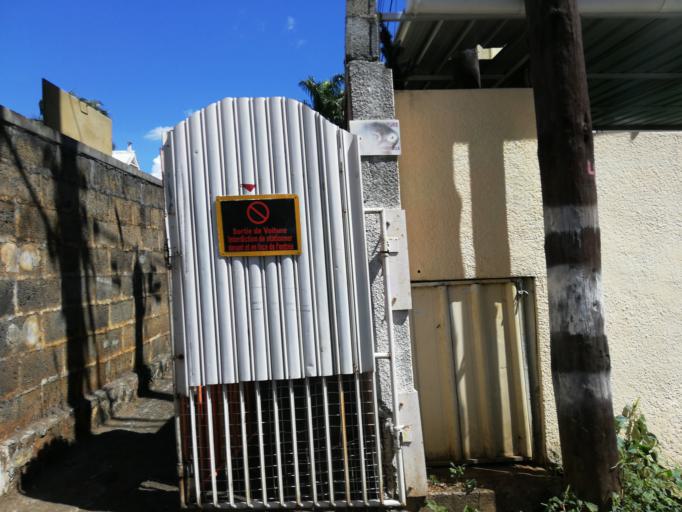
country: MU
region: Plaines Wilhems
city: Ebene
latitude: -20.2287
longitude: 57.4648
